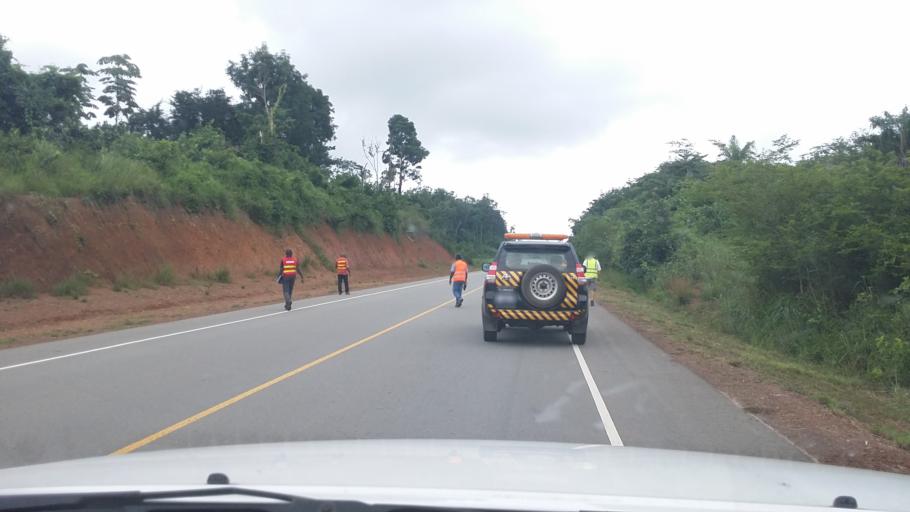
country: LR
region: Bong
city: Gbarnga
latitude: 7.0524
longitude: -9.2326
